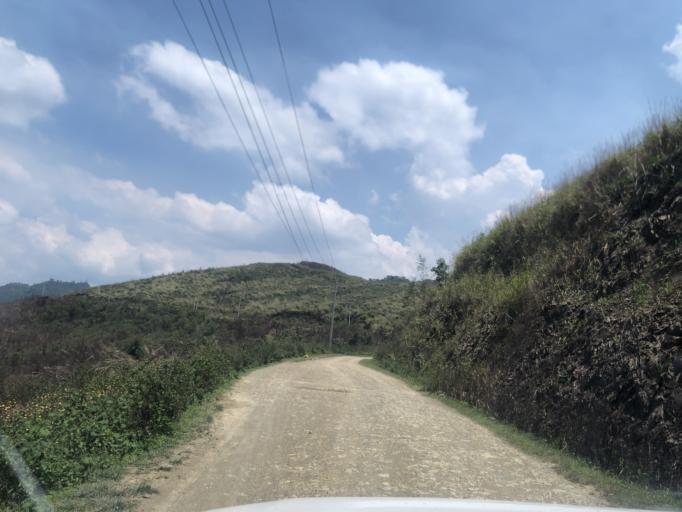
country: LA
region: Phongsali
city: Phongsali
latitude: 21.4045
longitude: 102.1857
